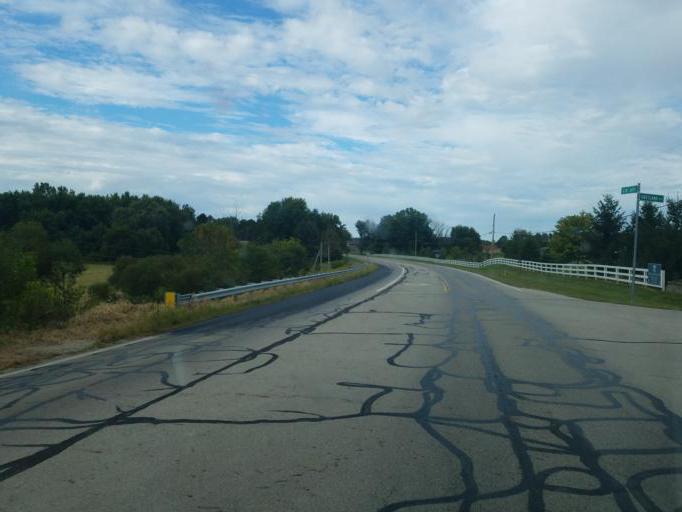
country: US
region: Ohio
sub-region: Delaware County
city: Sunbury
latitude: 40.2290
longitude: -82.7905
